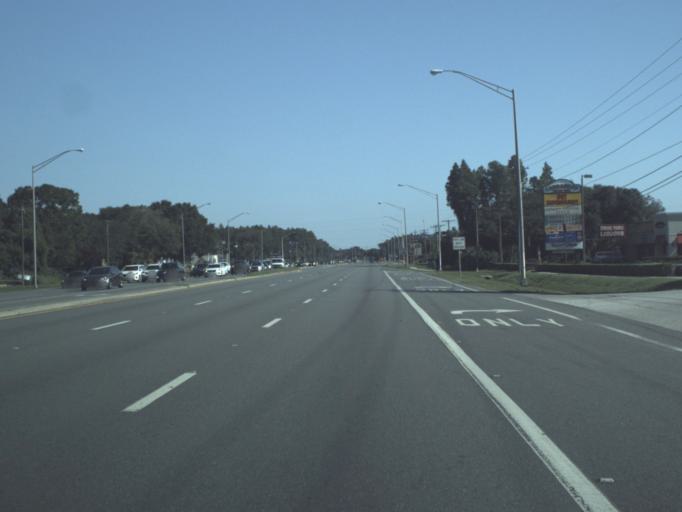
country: US
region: Florida
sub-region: Hillsborough County
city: Carrollwood
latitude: 28.0513
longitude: -82.5041
